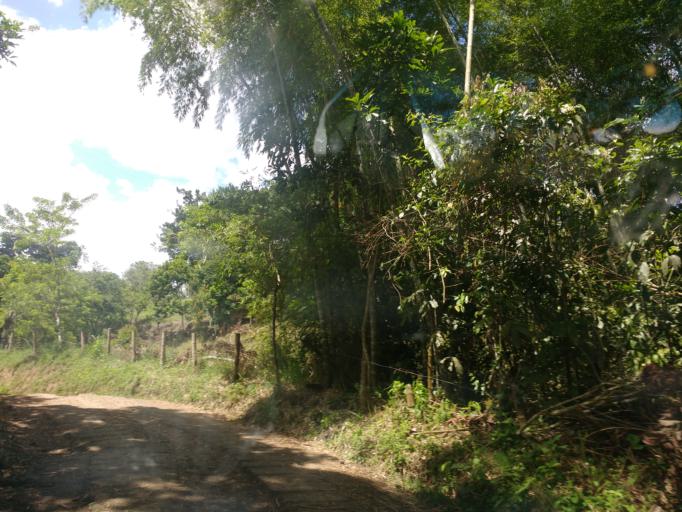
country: CO
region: Valle del Cauca
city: Alcala
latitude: 4.6792
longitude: -75.8049
